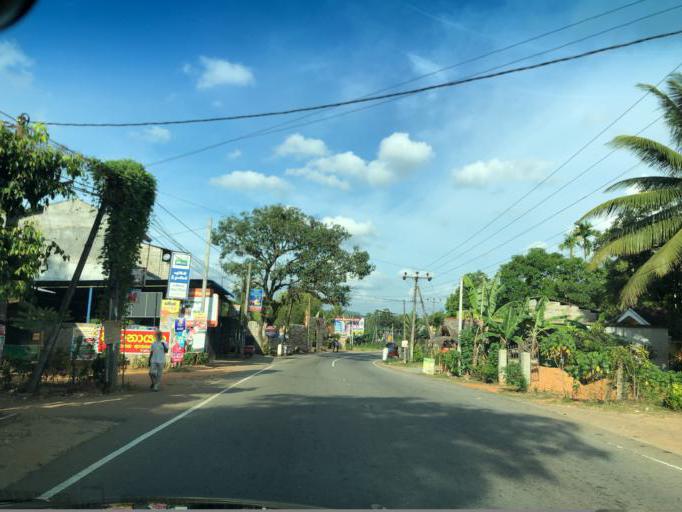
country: LK
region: Western
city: Horawala Junction
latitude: 6.5254
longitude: 80.0881
